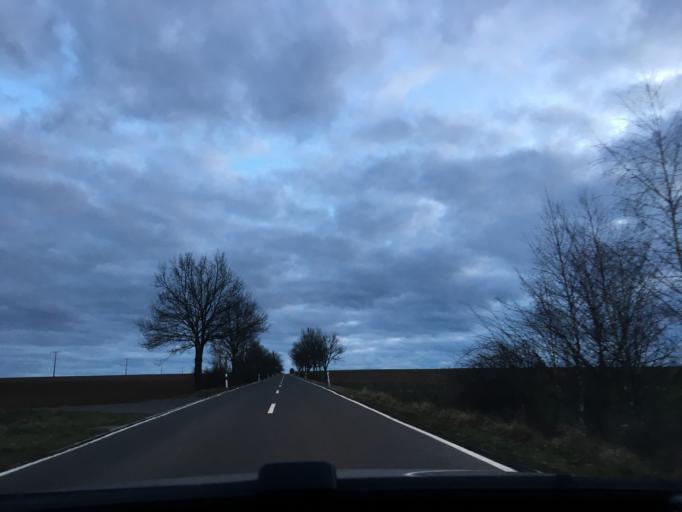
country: DE
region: Rheinland-Pfalz
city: Nack
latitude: 49.7451
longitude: 8.0035
